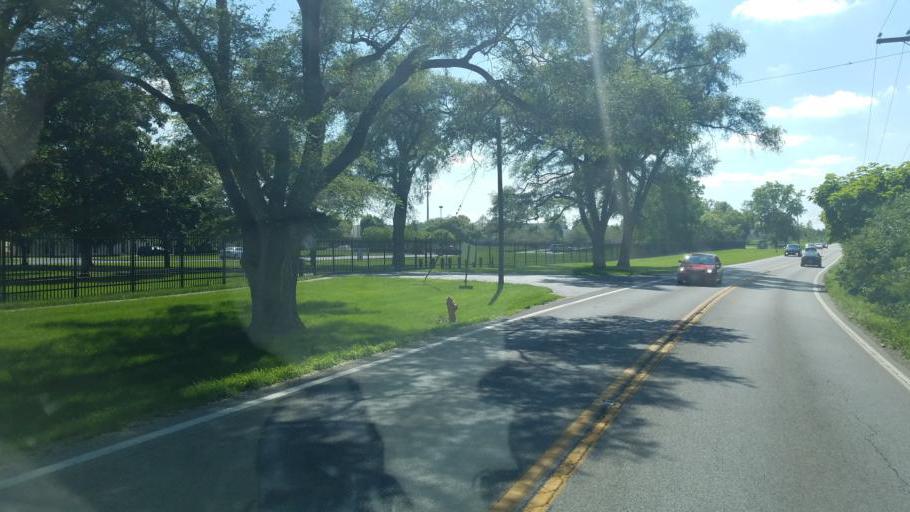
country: US
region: Ohio
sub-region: Franklin County
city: Worthington
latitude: 40.0906
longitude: -83.0661
